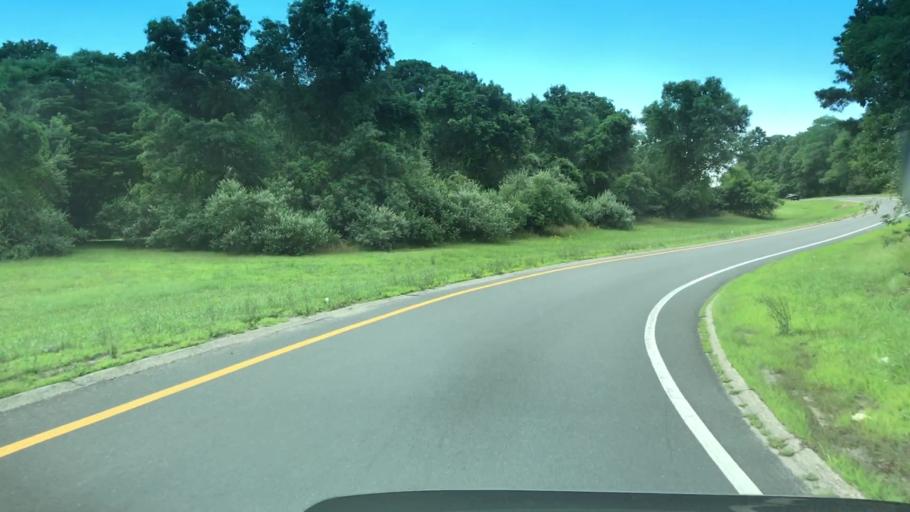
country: US
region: New York
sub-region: Suffolk County
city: Yaphank
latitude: 40.8456
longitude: -72.8926
